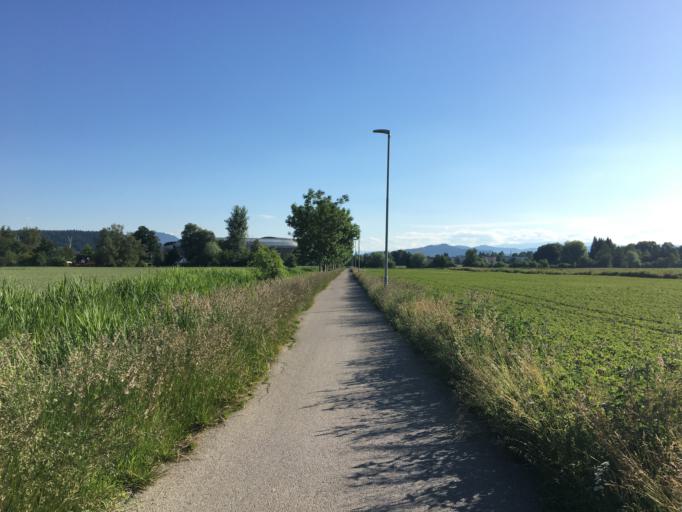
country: AT
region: Carinthia
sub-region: Klagenfurt am Woerthersee
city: Klagenfurt am Woerthersee
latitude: 46.6022
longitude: 14.2756
